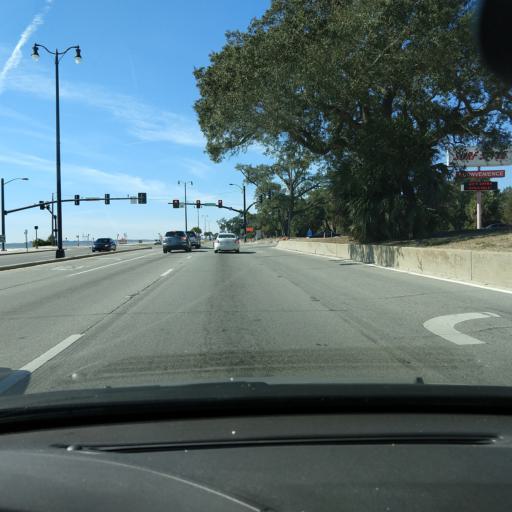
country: US
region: Mississippi
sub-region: Harrison County
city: Gulfport
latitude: 30.3788
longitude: -89.0433
